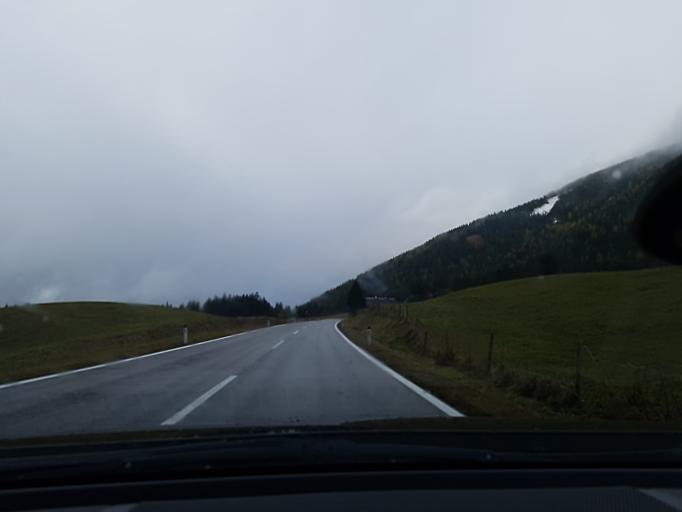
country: AT
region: Styria
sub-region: Politischer Bezirk Murtal
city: Hohentauern
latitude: 47.4042
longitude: 14.4635
